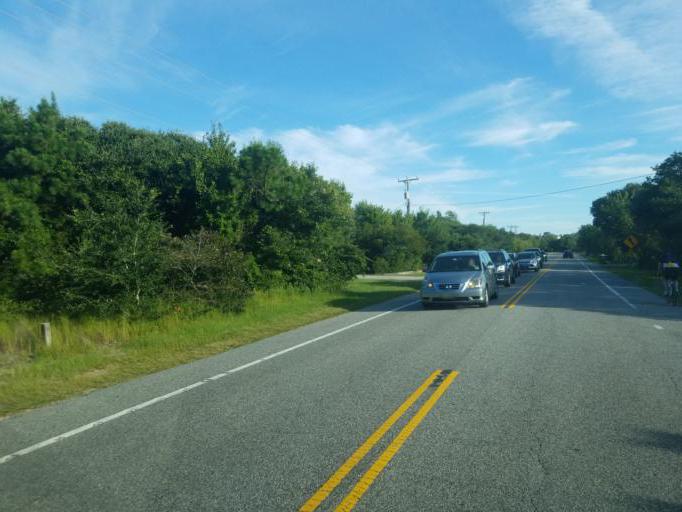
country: US
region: North Carolina
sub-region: Dare County
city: Southern Shores
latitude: 36.2950
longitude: -75.8027
